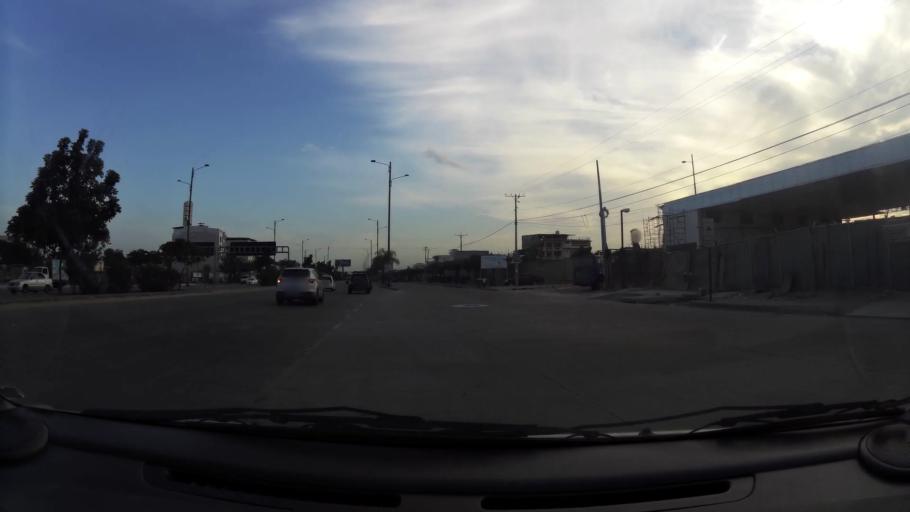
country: EC
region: Guayas
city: Eloy Alfaro
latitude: -2.1371
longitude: -79.8816
